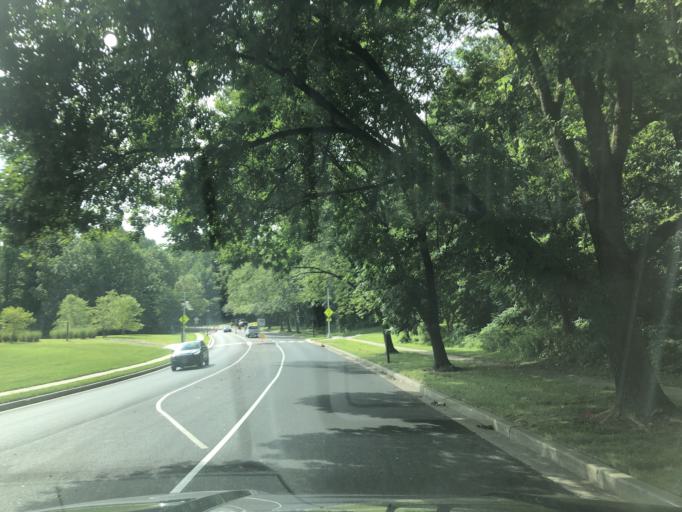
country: US
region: Maryland
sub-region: Howard County
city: Riverside
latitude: 39.2085
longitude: -76.8775
